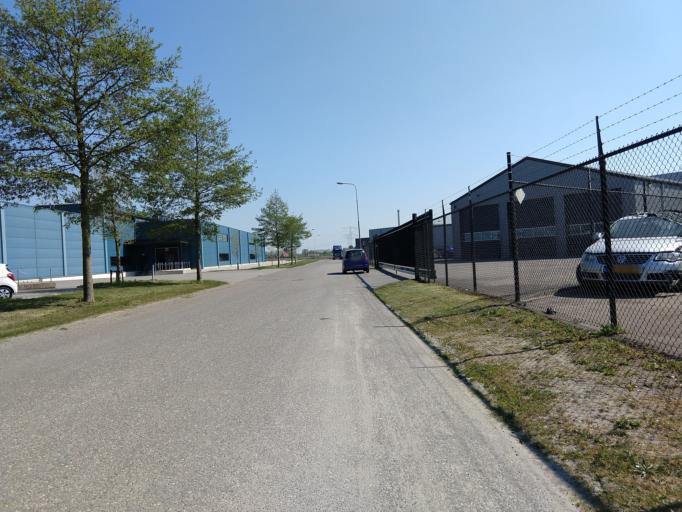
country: NL
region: Zeeland
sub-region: Gemeente Reimerswaal
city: Yerseke
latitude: 51.4709
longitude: 3.9817
